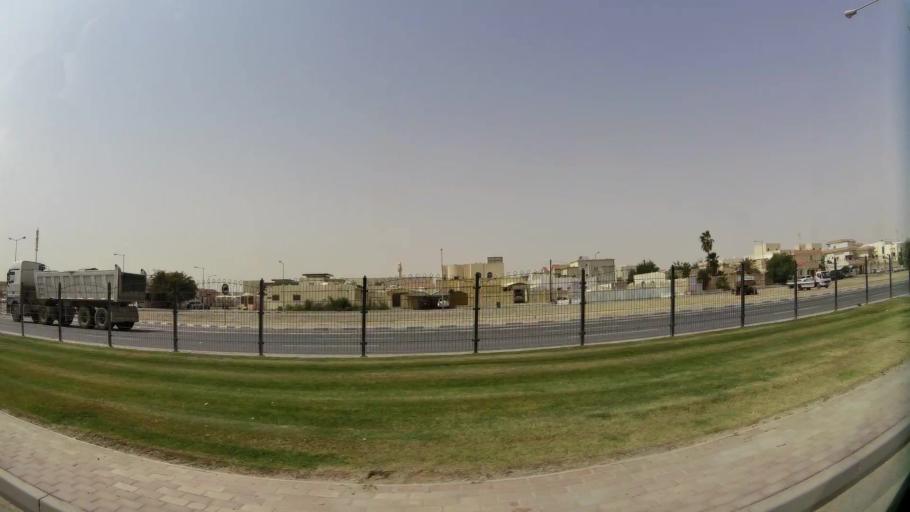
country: QA
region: Baladiyat ar Rayyan
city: Ar Rayyan
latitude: 25.2462
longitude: 51.4313
